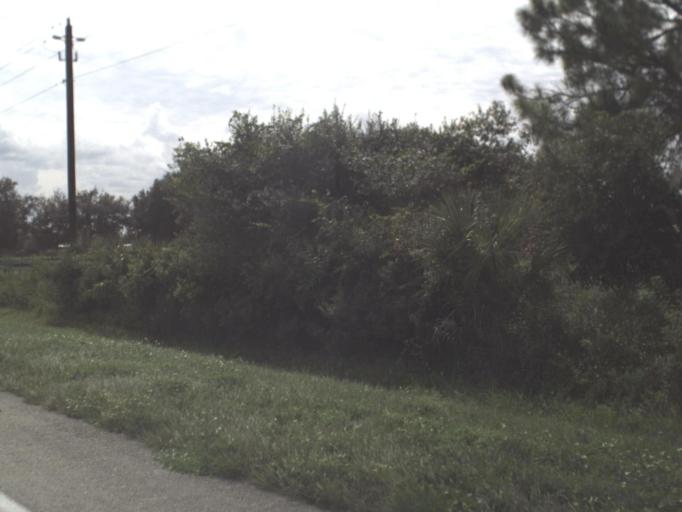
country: US
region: Florida
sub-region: DeSoto County
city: Nocatee
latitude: 27.0754
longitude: -81.7953
